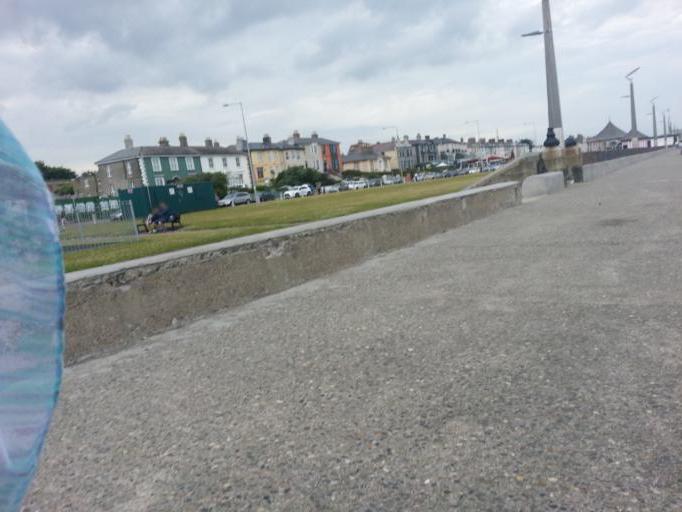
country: IE
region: Leinster
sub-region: Wicklow
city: Bray
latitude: 53.2006
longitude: -6.0961
